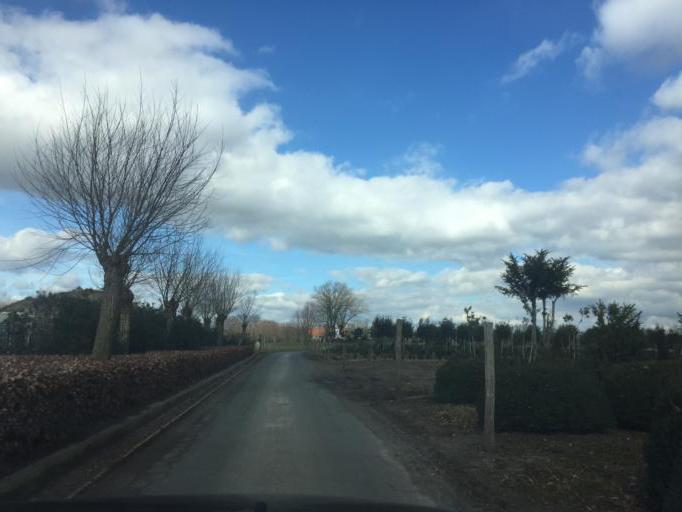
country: BE
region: Flanders
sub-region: Provincie West-Vlaanderen
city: Ardooie
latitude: 50.9866
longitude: 3.1560
